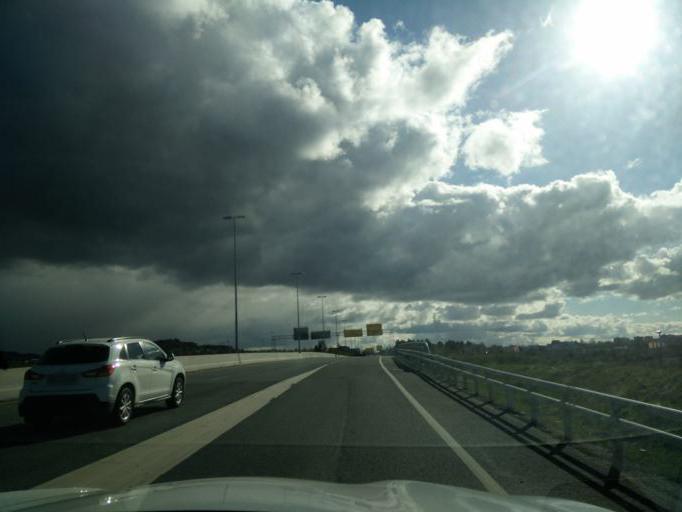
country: NO
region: Sor-Trondelag
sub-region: Trondheim
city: Trondheim
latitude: 63.4297
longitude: 10.4847
